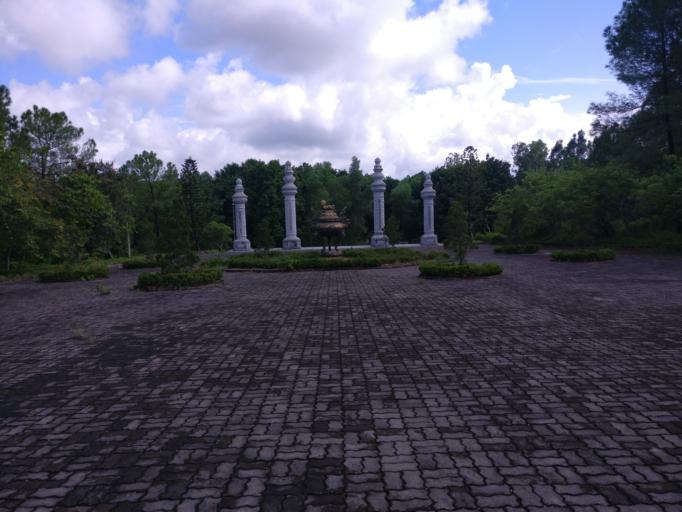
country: VN
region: Thua Thien-Hue
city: Hue
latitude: 16.4188
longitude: 107.6094
